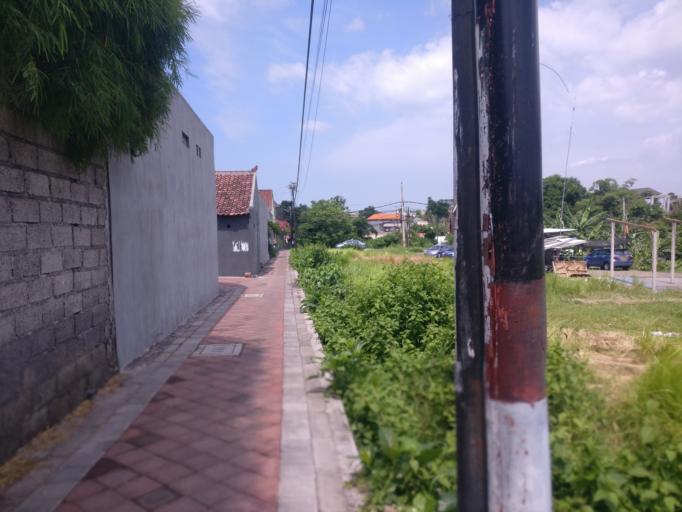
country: ID
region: Bali
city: Kuta
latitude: -8.6782
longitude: 115.1614
